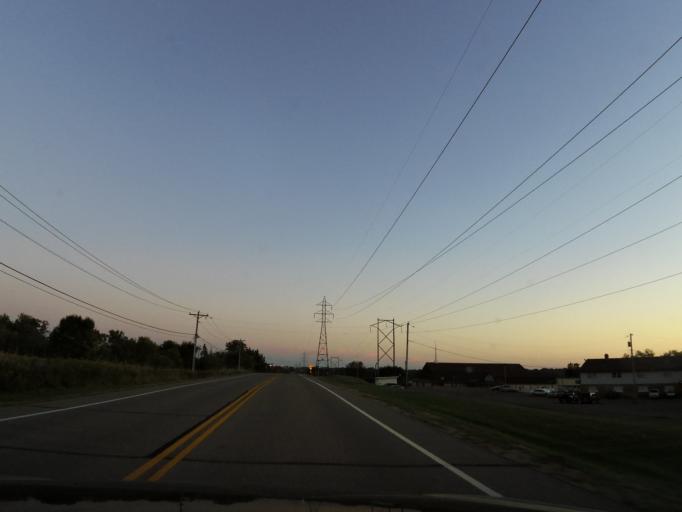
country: US
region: Minnesota
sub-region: Washington County
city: Oakdale
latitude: 44.9517
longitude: -92.9644
